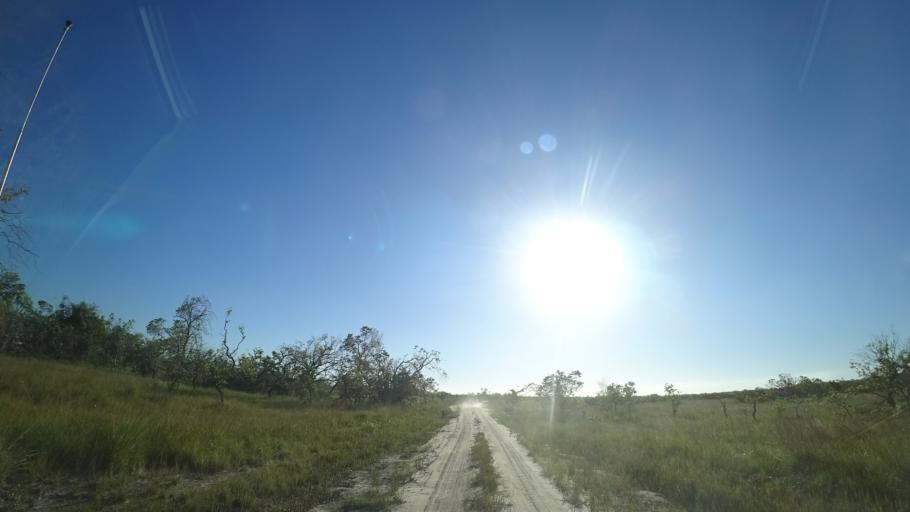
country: MZ
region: Sofala
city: Beira
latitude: -19.5724
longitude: 35.2371
